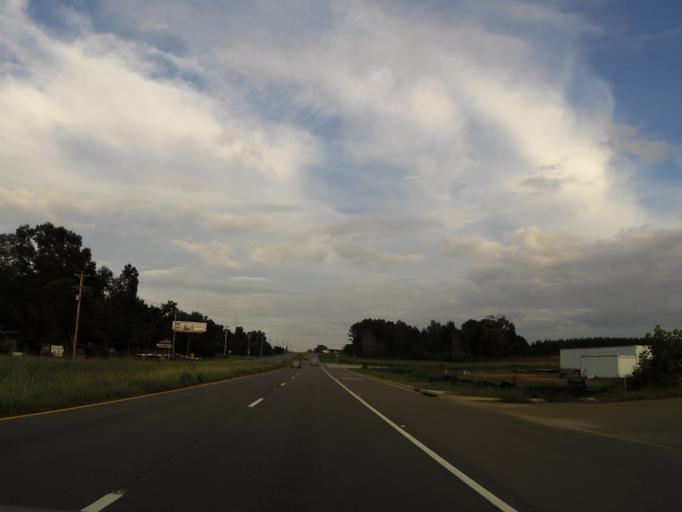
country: US
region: Alabama
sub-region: Madison County
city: Madison
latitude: 34.7507
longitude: -86.8160
